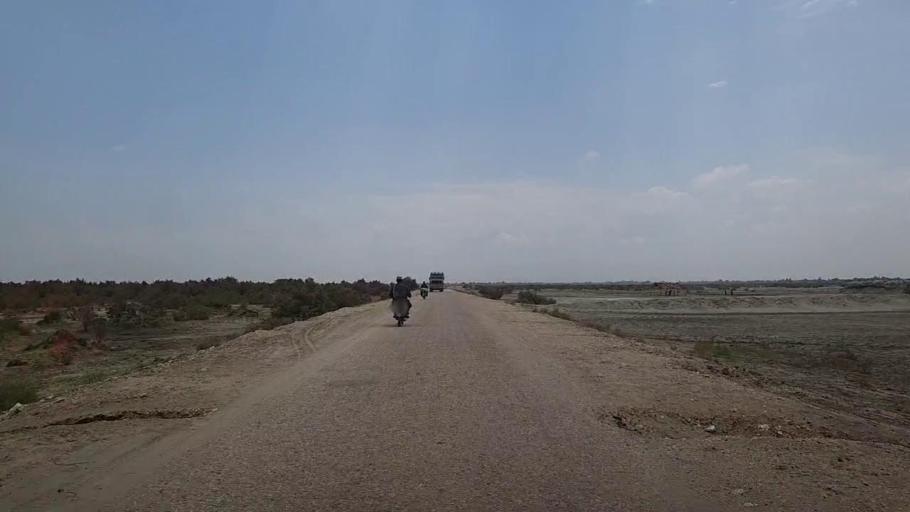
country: PK
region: Sindh
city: Kandhkot
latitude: 28.2885
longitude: 69.1488
